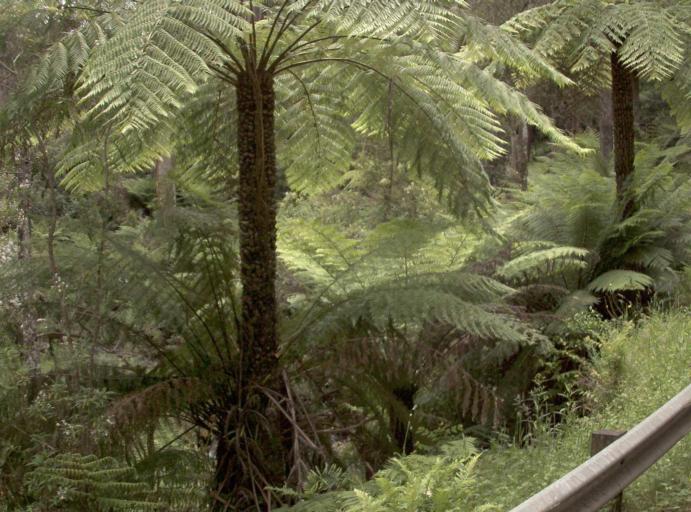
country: AU
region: Victoria
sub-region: Latrobe
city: Traralgon
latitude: -38.4658
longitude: 146.5520
